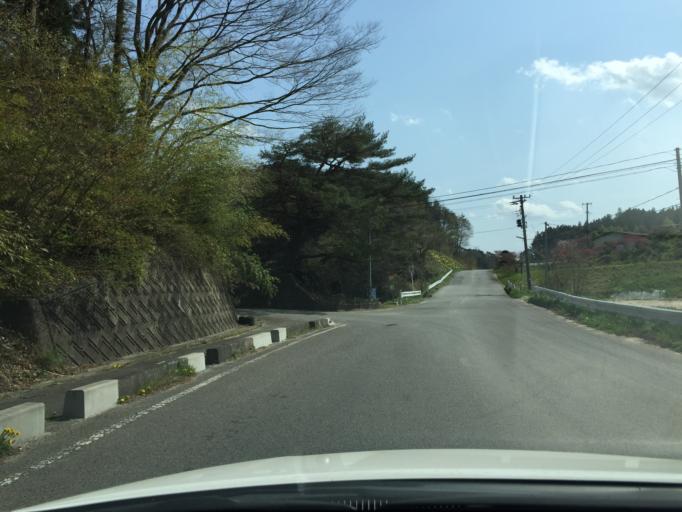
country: JP
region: Fukushima
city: Namie
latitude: 37.4002
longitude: 140.8019
